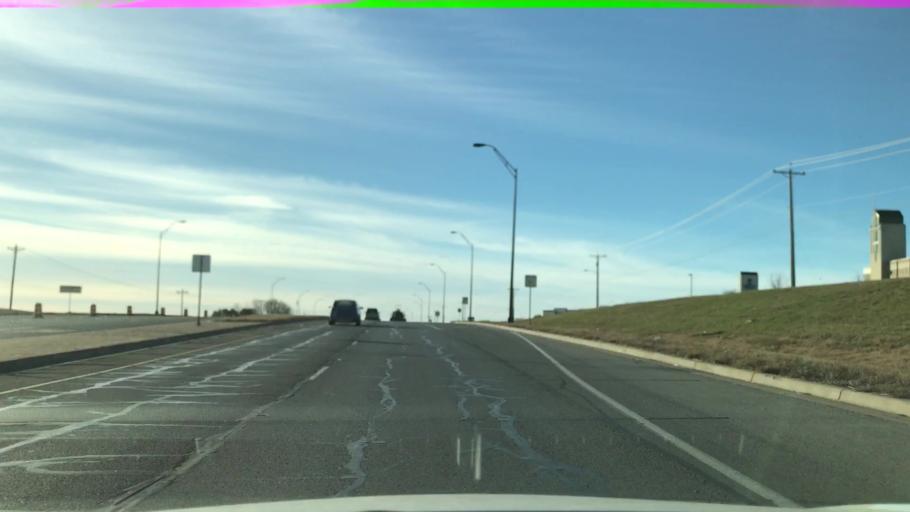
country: US
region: Texas
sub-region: Williamson County
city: Georgetown
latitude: 30.5705
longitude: -97.6500
